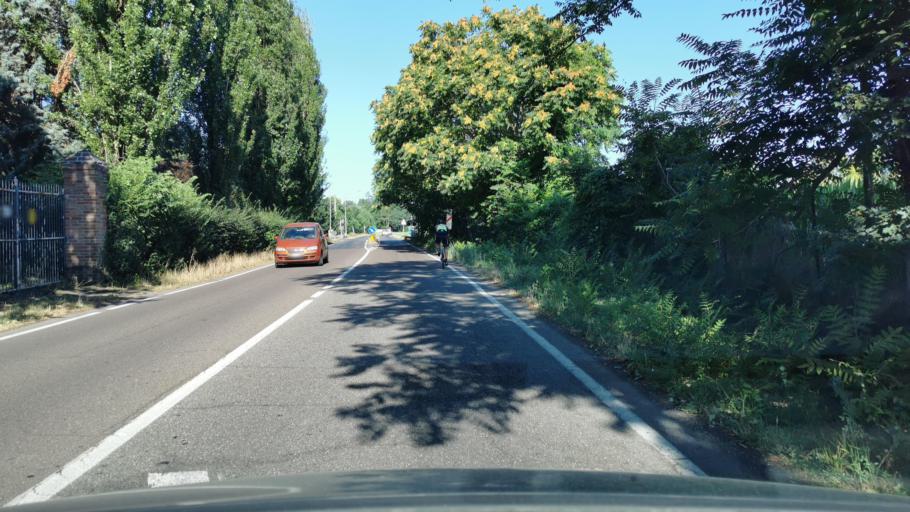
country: IT
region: Emilia-Romagna
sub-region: Provincia di Modena
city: Baggiovara
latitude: 44.6194
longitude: 10.8980
